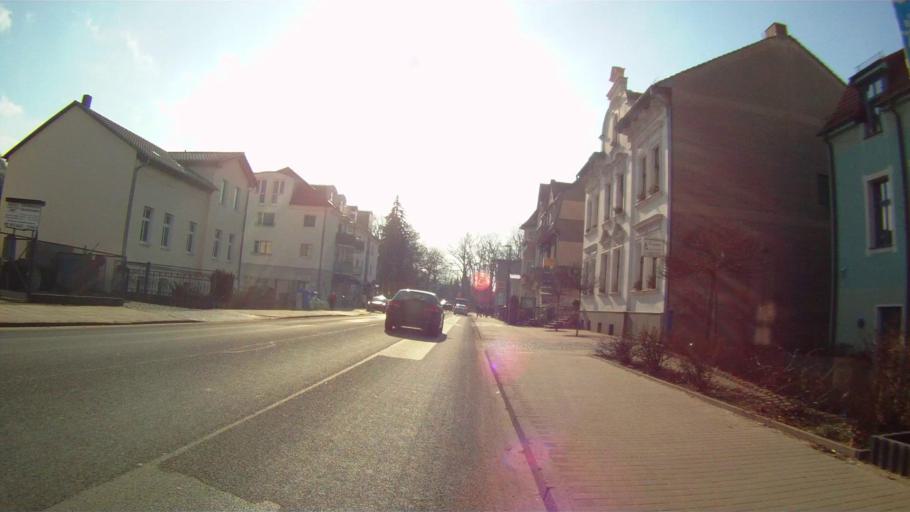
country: DE
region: Brandenburg
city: Erkner
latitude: 52.4183
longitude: 13.7541
